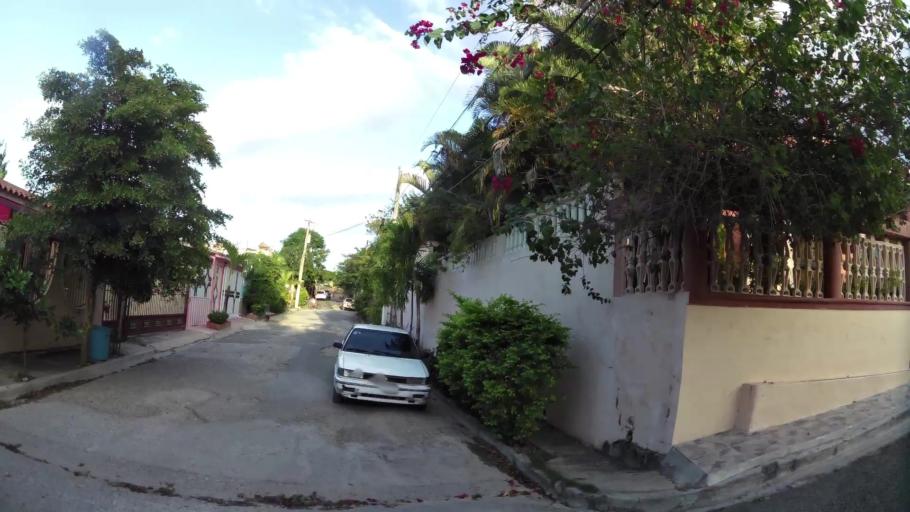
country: DO
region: Nacional
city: La Agustina
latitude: 18.5555
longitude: -69.9251
